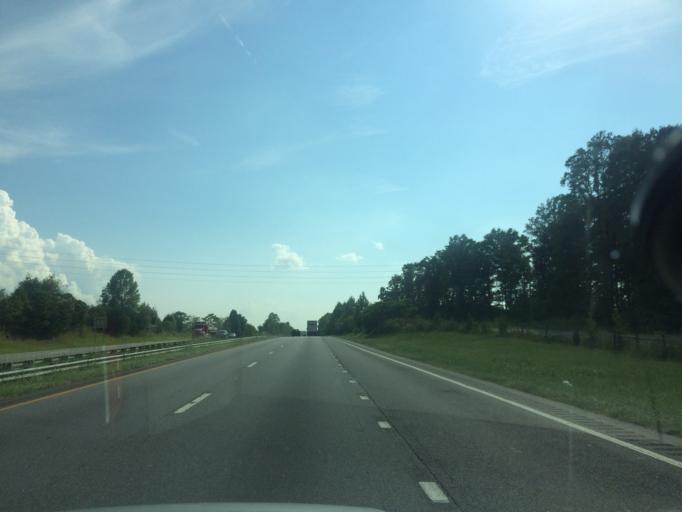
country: US
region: North Carolina
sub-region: Cleveland County
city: Kings Mountain
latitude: 35.2234
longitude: -81.3366
